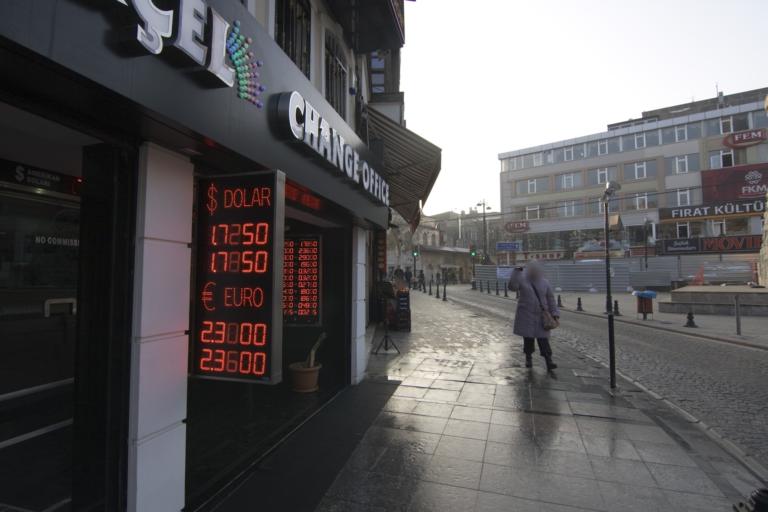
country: TR
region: Istanbul
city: Eminoenue
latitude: 41.0087
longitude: 28.9714
